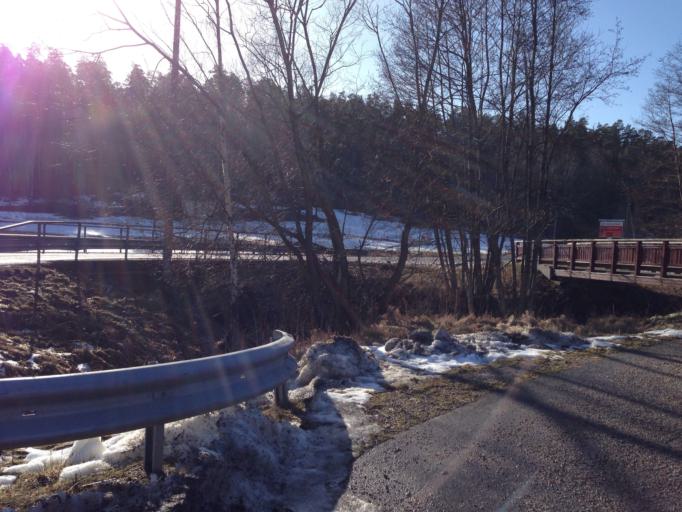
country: SE
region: Stockholm
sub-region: Botkyrka Kommun
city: Varsta
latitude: 59.1559
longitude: 17.8194
